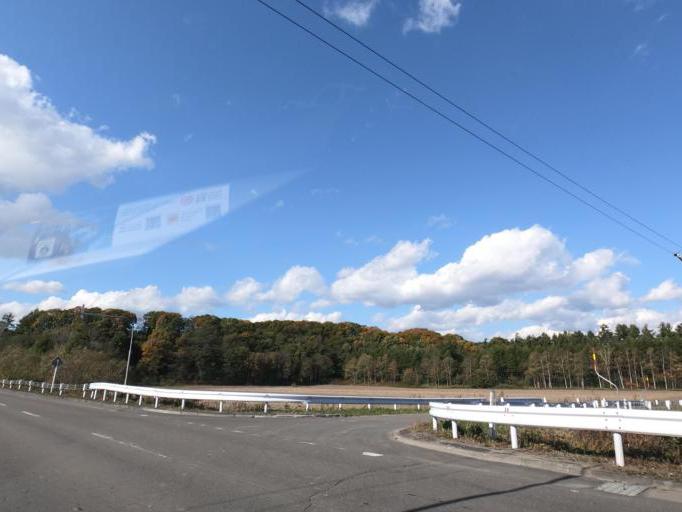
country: JP
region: Hokkaido
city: Otofuke
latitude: 43.2387
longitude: 143.2692
